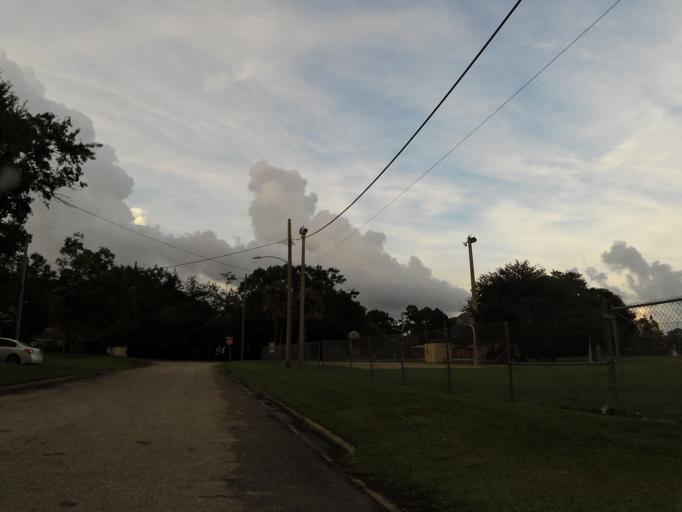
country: US
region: Florida
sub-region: Duval County
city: Jacksonville
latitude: 30.3481
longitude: -81.7023
